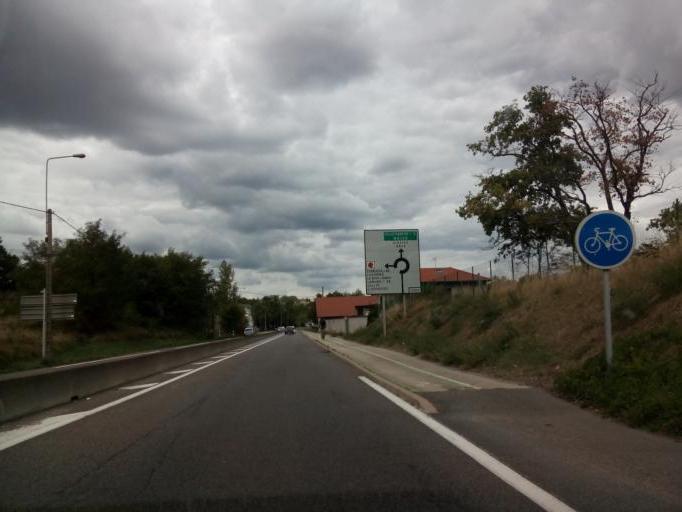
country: FR
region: Rhone-Alpes
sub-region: Departement du Rhone
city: Lissieu
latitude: 45.8422
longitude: 4.7361
